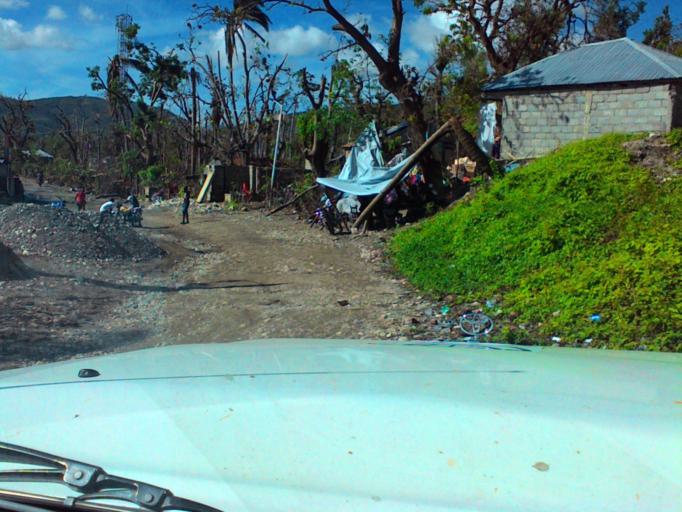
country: HT
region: Grandans
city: Jeremie
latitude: 18.6123
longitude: -74.0836
